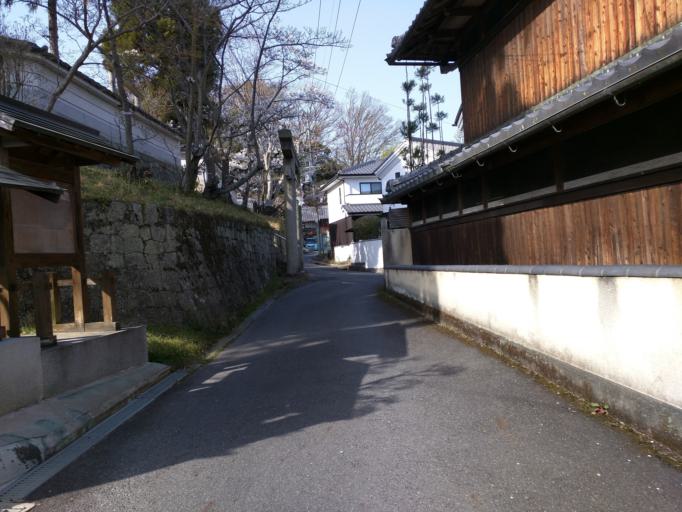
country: JP
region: Kyoto
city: Tanabe
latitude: 34.7670
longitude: 135.7833
